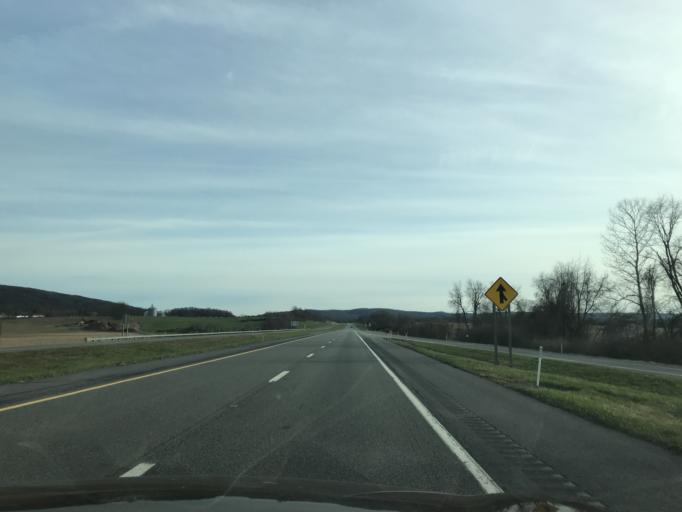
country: US
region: Pennsylvania
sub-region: Union County
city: Lewisburg
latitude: 40.9632
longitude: -76.8449
